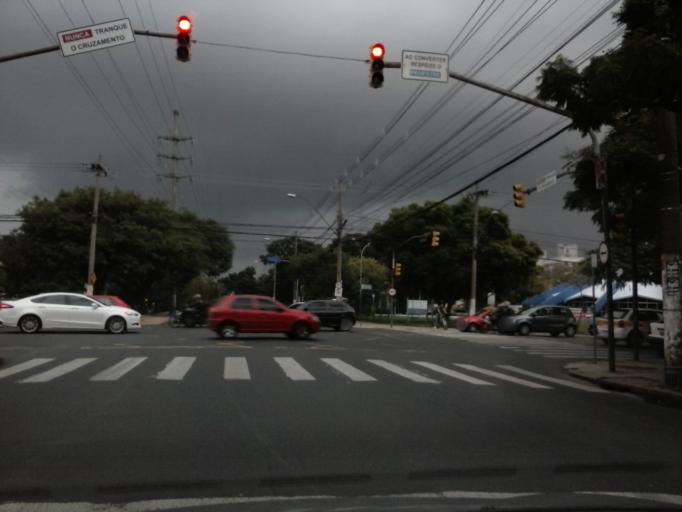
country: BR
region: Rio Grande do Sul
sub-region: Porto Alegre
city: Porto Alegre
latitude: -30.0438
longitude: -51.2069
